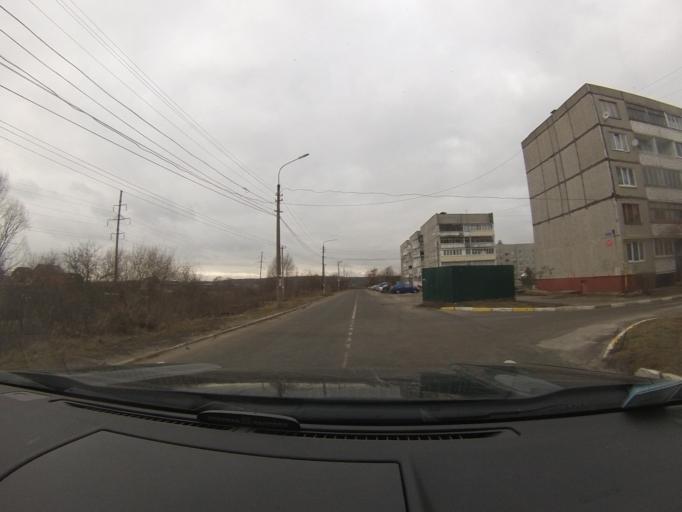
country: RU
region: Moskovskaya
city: Lopatinskiy
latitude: 55.3345
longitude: 38.7100
